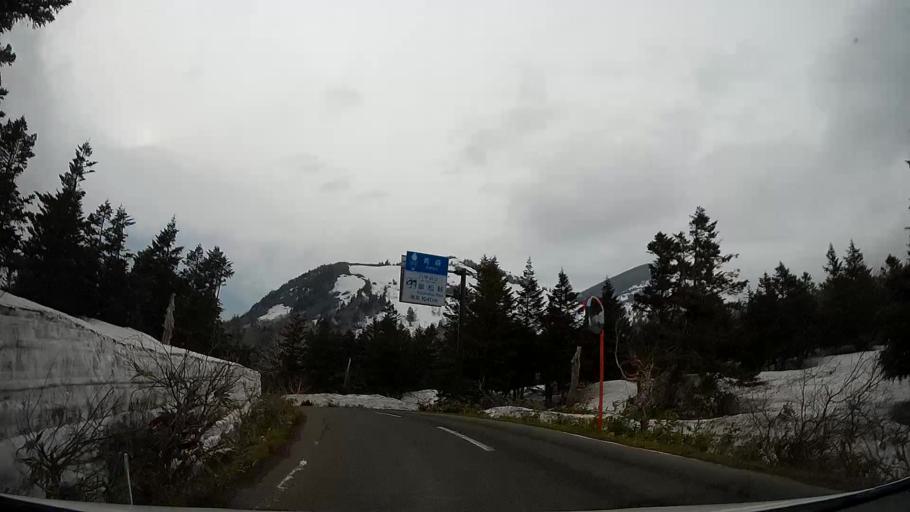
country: JP
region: Aomori
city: Aomori Shi
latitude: 40.6344
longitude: 140.8828
